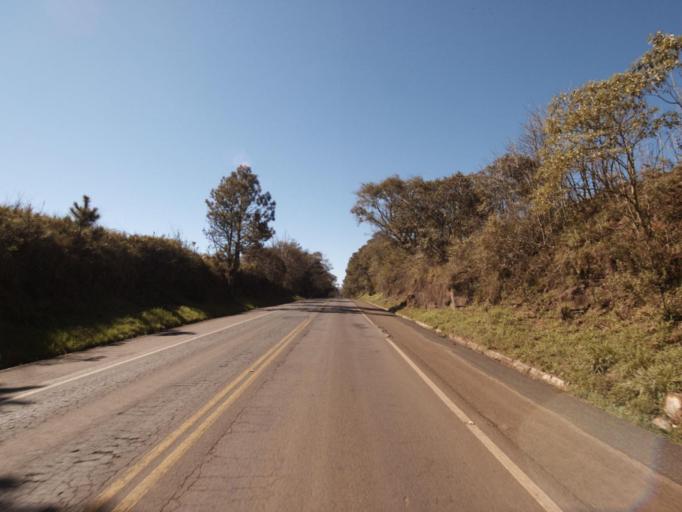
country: BR
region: Santa Catarina
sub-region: Sao Lourenco Do Oeste
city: Sao Lourenco dOeste
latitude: -26.8294
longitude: -53.1205
